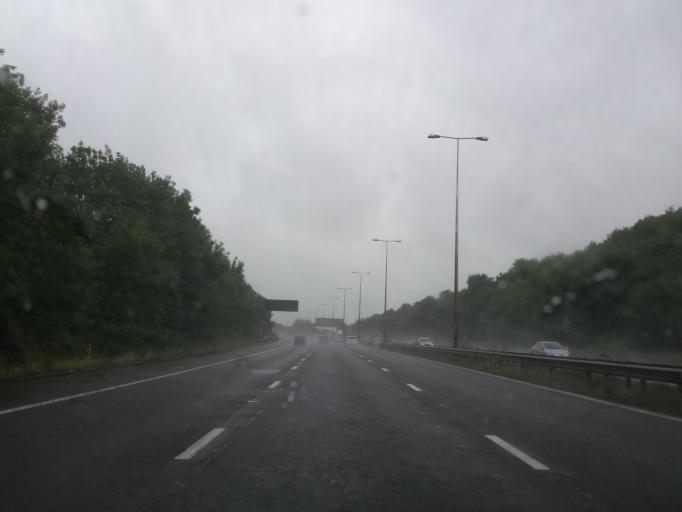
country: GB
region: England
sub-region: Leicestershire
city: Kegworth
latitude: 52.8074
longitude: -1.3048
